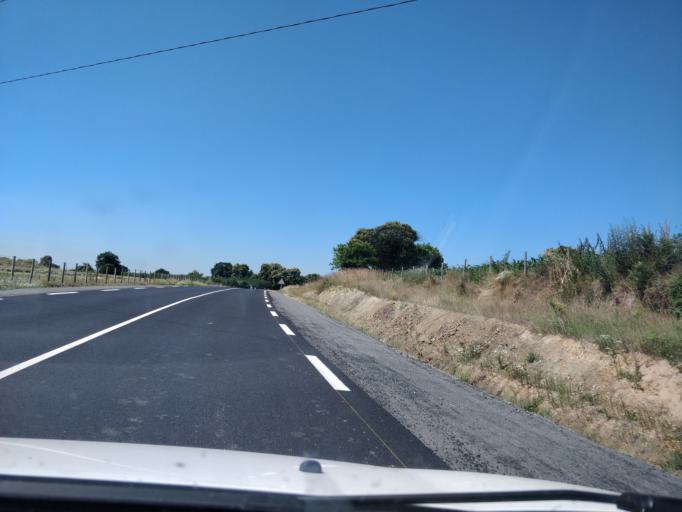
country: FR
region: Brittany
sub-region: Departement d'Ille-et-Vilaine
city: Dol-de-Bretagne
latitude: 48.5383
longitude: -1.7328
